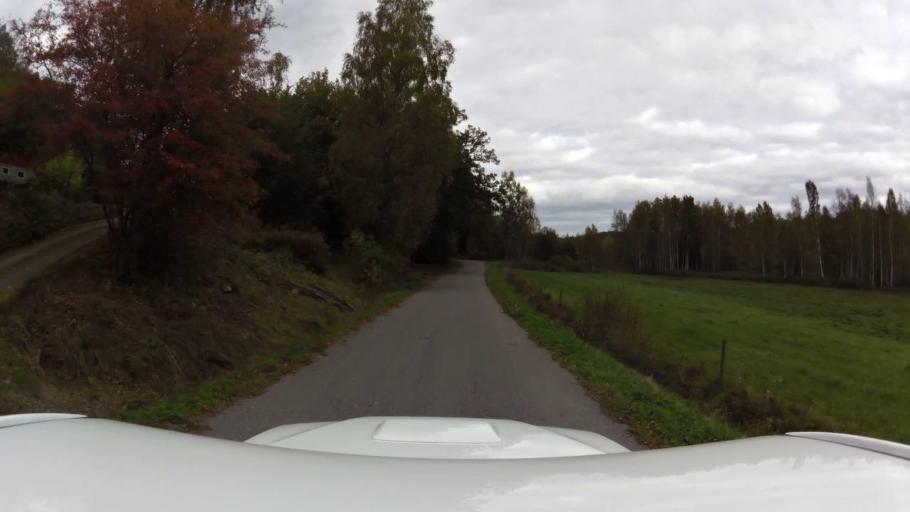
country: SE
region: OEstergoetland
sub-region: Kinda Kommun
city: Rimforsa
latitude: 58.2000
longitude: 15.5608
